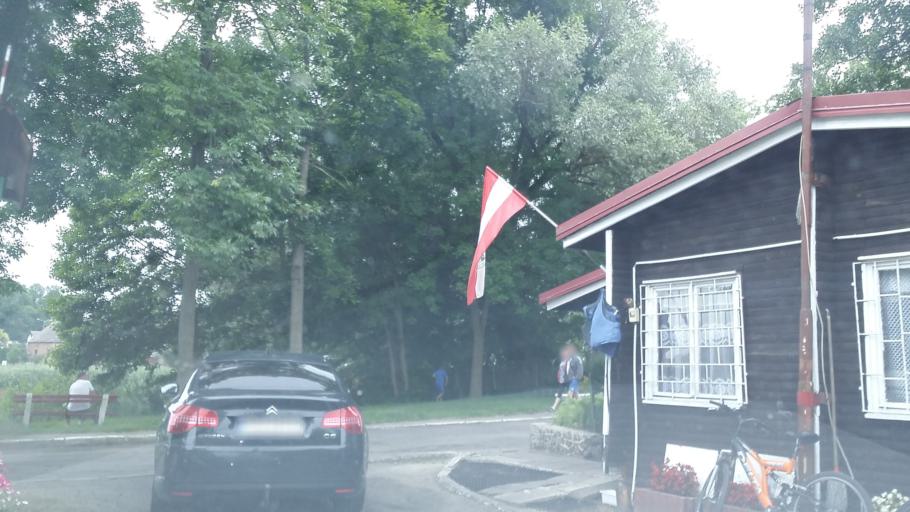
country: PL
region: West Pomeranian Voivodeship
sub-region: Powiat choszczenski
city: Drawno
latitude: 53.2168
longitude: 15.7639
